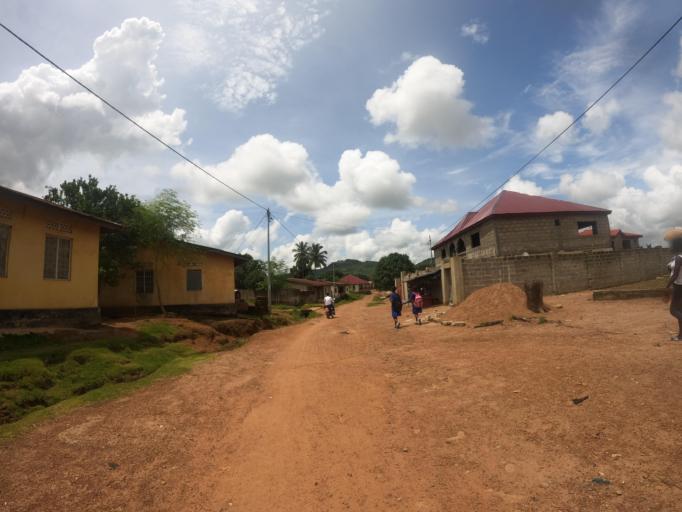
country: SL
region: Northern Province
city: Makeni
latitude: 8.8936
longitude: -12.0506
